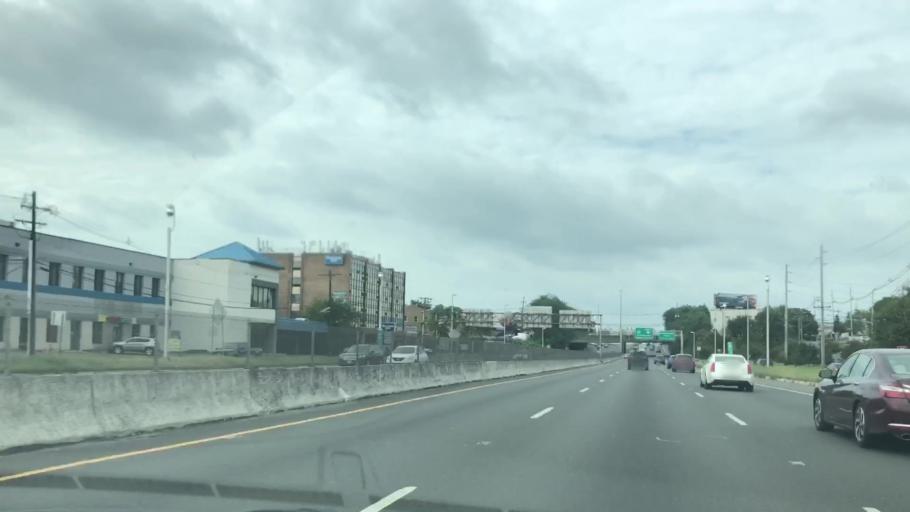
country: US
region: New Jersey
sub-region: Hudson County
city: Secaucus
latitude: 40.7925
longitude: -74.0557
